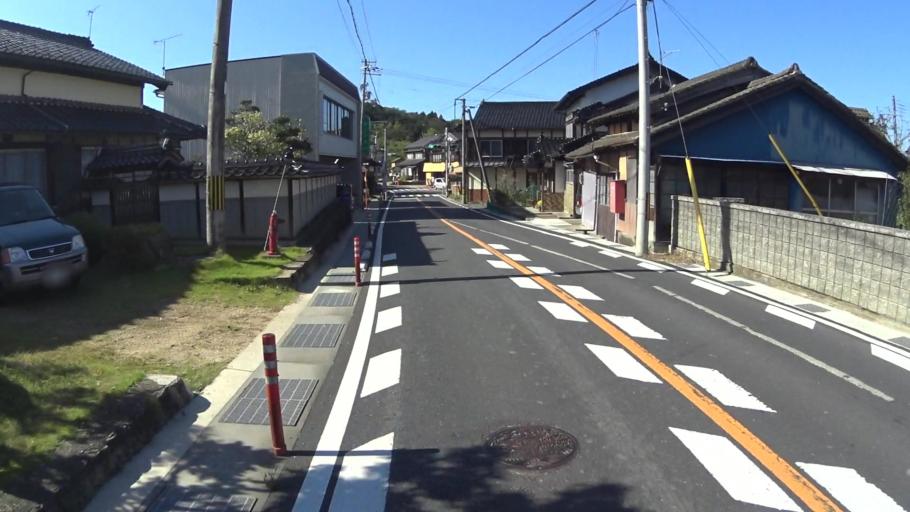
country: JP
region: Hyogo
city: Toyooka
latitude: 35.5833
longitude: 134.9622
